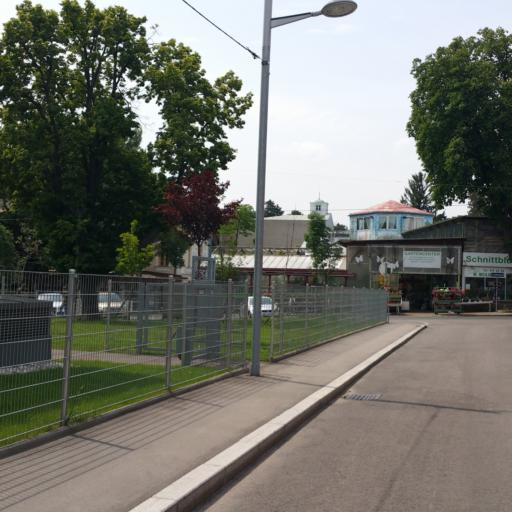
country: AT
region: Vienna
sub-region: Wien Stadt
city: Vienna
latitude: 48.2147
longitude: 16.3009
